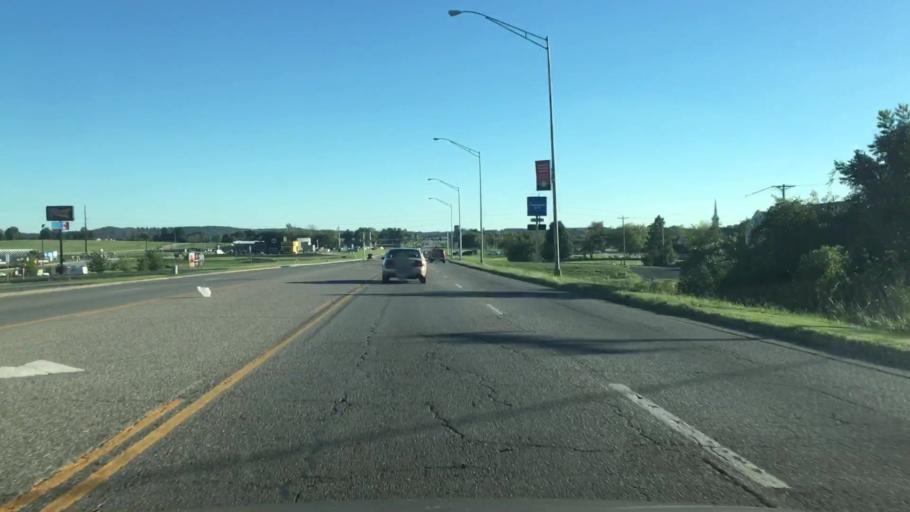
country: US
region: Oklahoma
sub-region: Cherokee County
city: Park Hill
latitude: 35.8805
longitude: -94.9763
